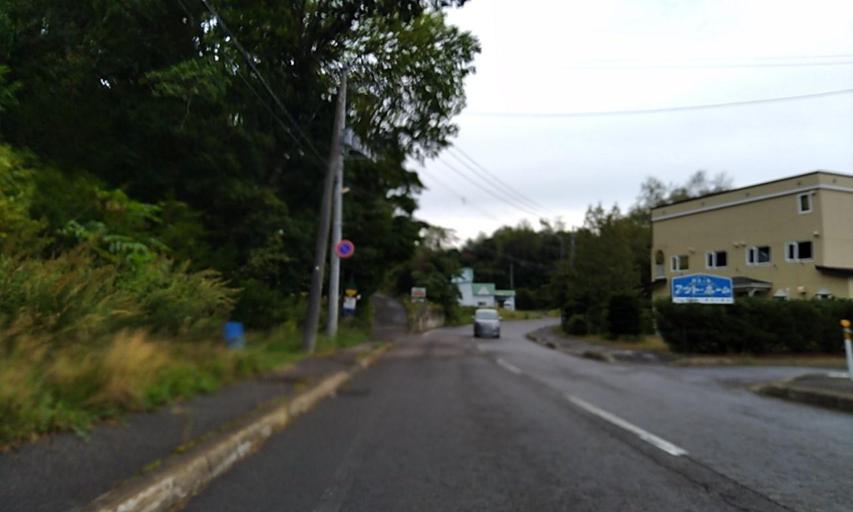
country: JP
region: Hokkaido
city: Abashiri
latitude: 44.0029
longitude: 144.2312
